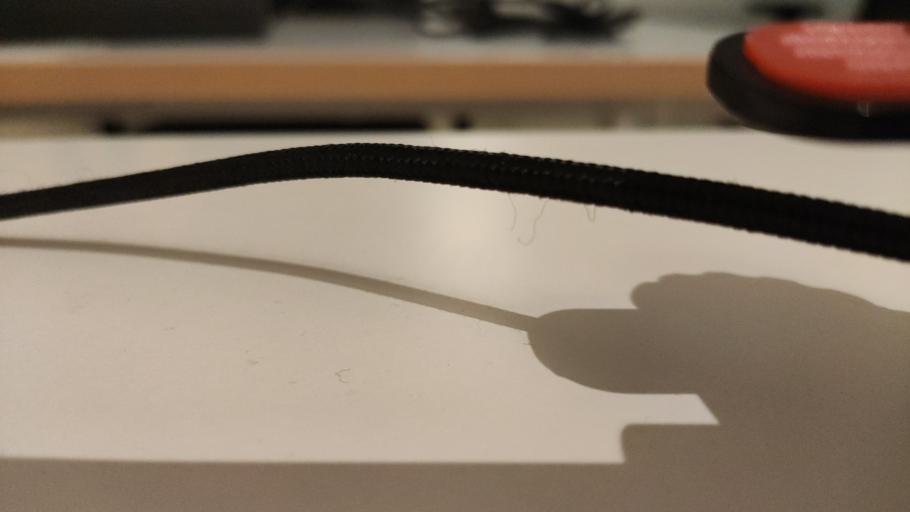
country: RU
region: Moskovskaya
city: Budenovetc
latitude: 56.3881
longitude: 37.6249
